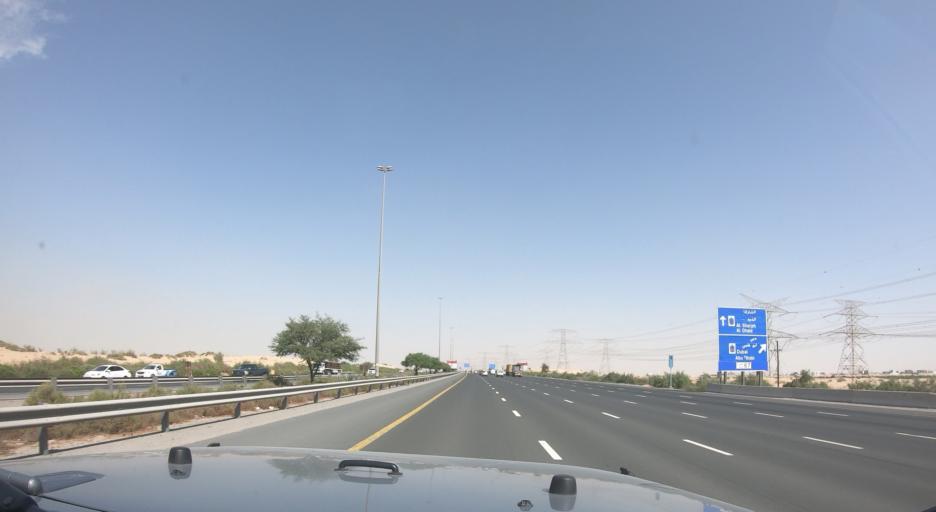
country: AE
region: Ash Shariqah
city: Sharjah
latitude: 25.1993
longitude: 55.5426
